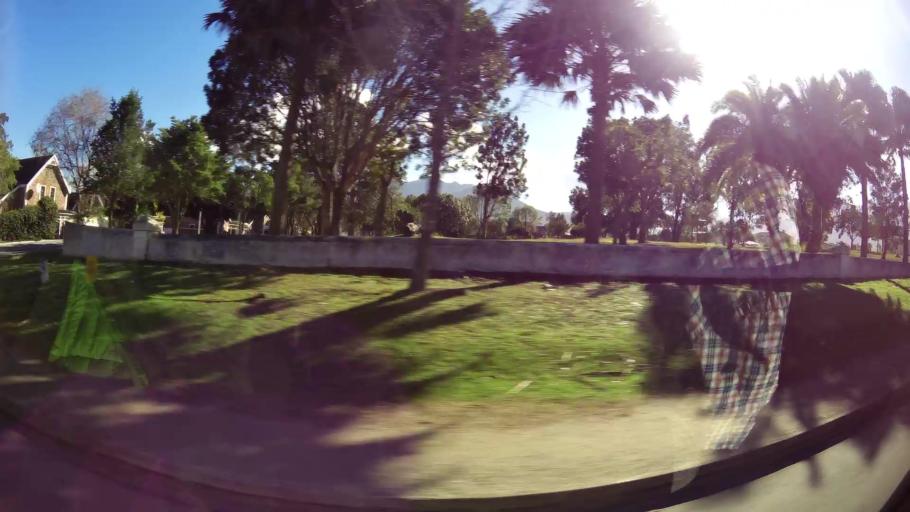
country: ZA
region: Western Cape
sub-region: Eden District Municipality
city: George
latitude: -33.9520
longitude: 22.4047
